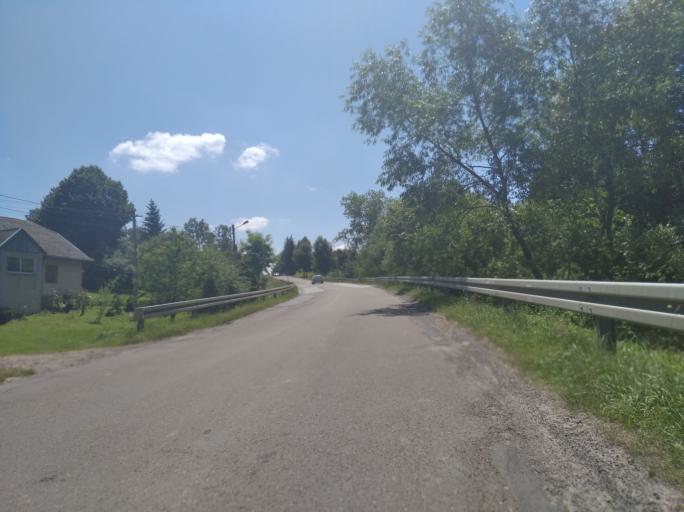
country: PL
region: Subcarpathian Voivodeship
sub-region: Powiat brzozowski
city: Jablonka
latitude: 49.6905
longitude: 22.1153
